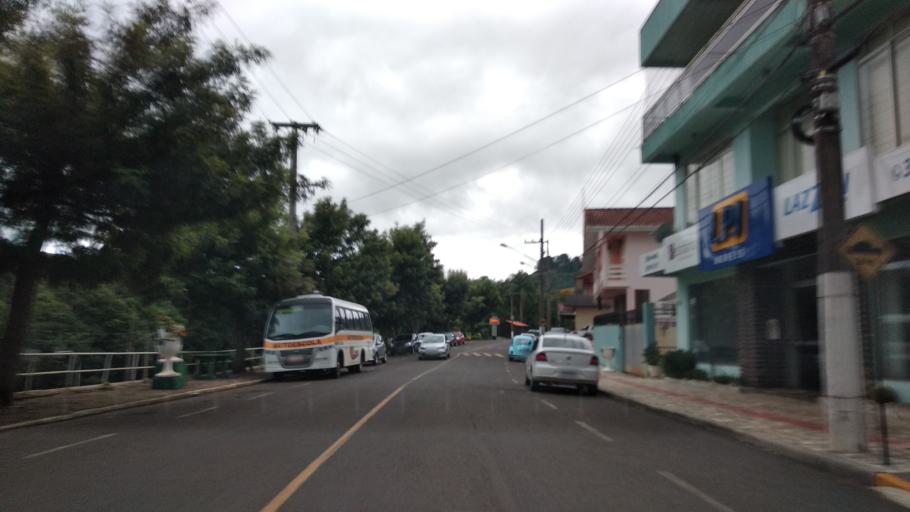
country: BR
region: Santa Catarina
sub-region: Videira
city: Videira
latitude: -27.0463
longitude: -51.2289
